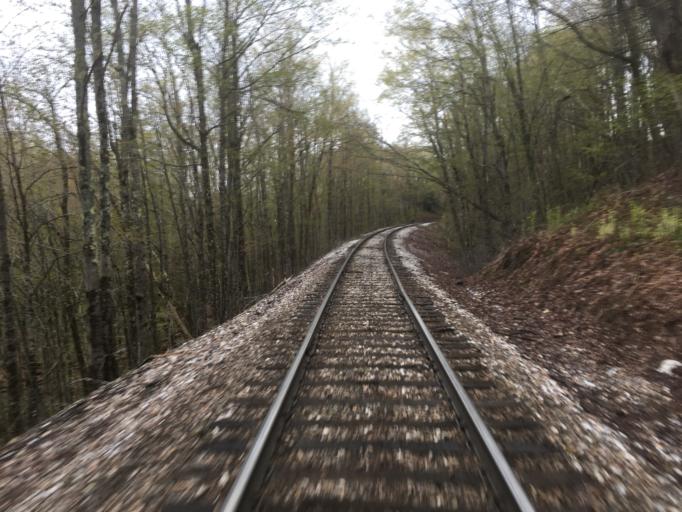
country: US
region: Vermont
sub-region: Rutland County
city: Rutland
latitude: 43.4594
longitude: -72.8766
